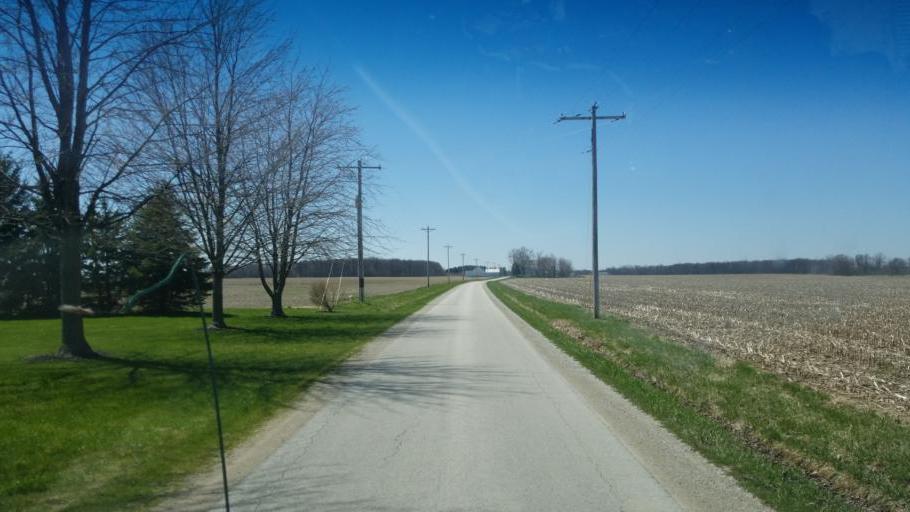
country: US
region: Ohio
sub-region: Huron County
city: Willard
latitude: 41.0445
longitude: -82.8622
